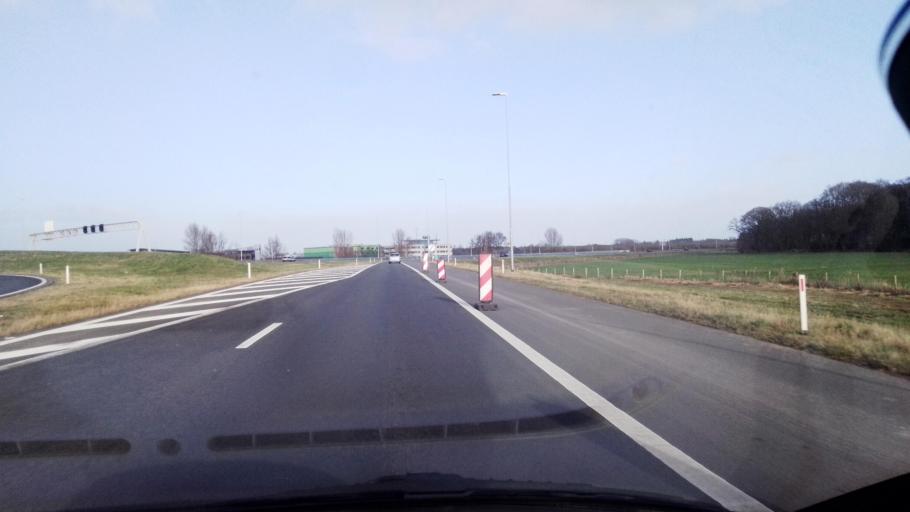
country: NL
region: Gelderland
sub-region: Gemeente Lochem
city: Epse
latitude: 52.2353
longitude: 6.2158
